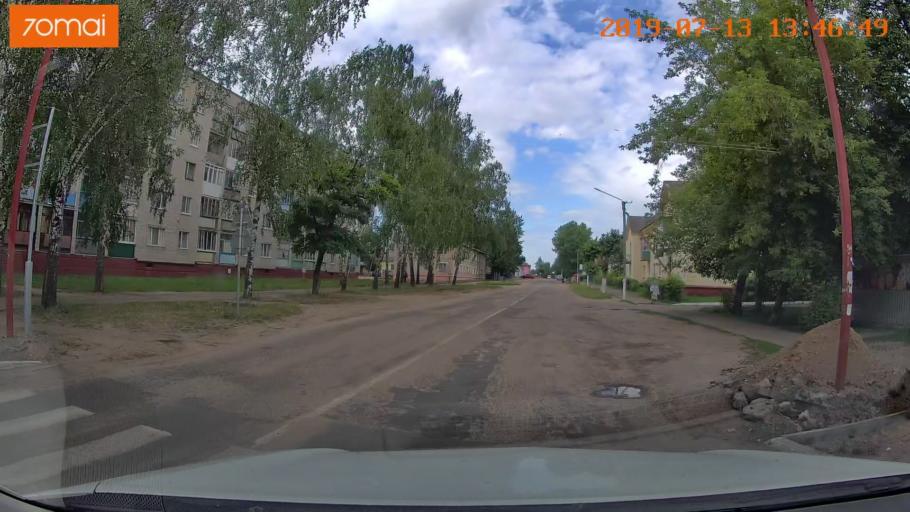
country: BY
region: Mogilev
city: Asipovichy
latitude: 53.2952
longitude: 28.6364
